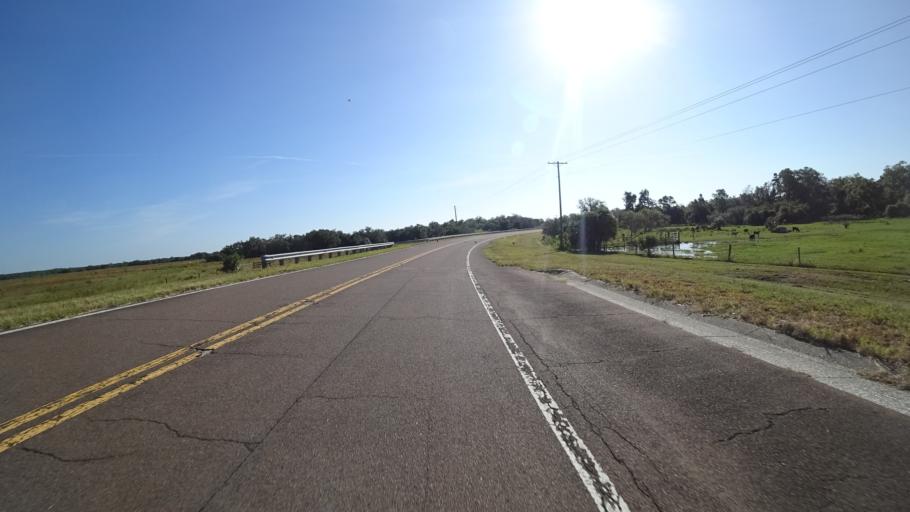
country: US
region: Florida
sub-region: Hillsborough County
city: Ruskin
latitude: 27.6575
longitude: -82.4350
